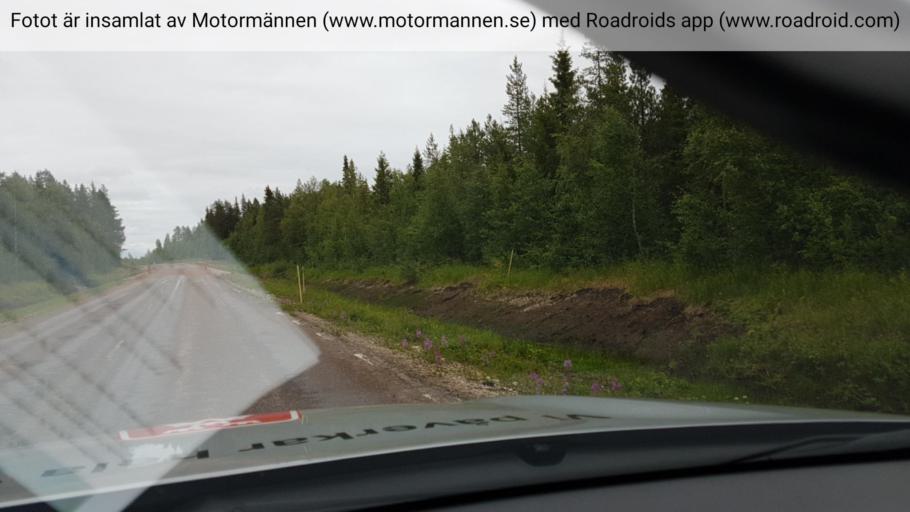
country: SE
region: Norrbotten
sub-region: Overkalix Kommun
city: OEverkalix
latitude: 67.0560
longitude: 22.3183
